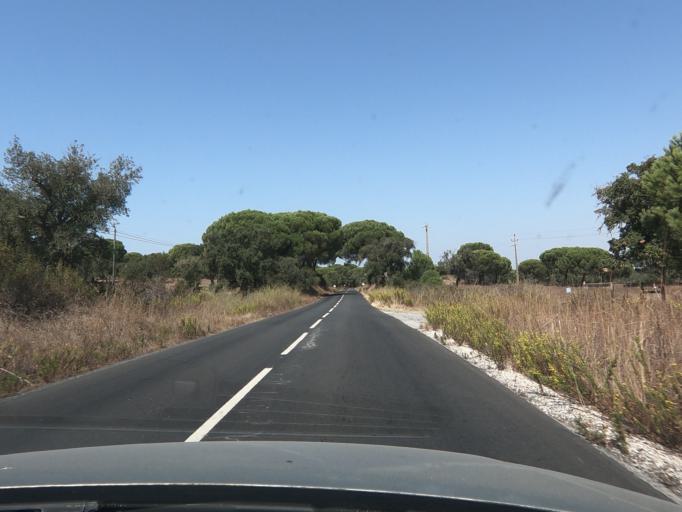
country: PT
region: Setubal
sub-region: Alcacer do Sal
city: Alcacer do Sal
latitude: 38.3366
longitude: -8.4426
